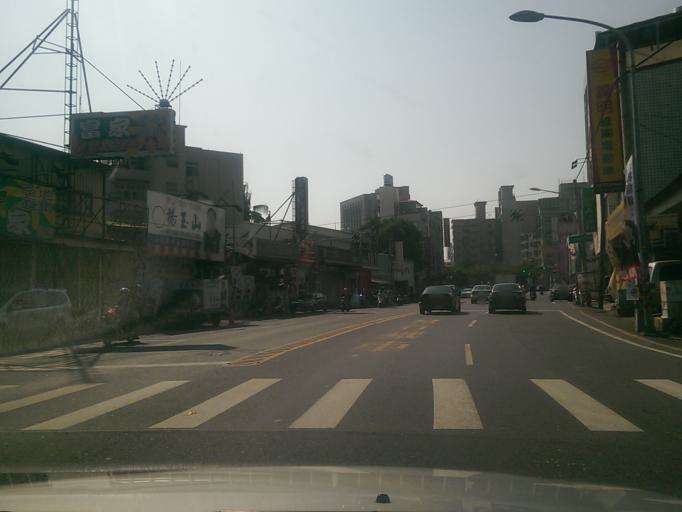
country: TW
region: Taiwan
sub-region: Changhua
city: Chang-hua
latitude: 24.0830
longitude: 120.5488
